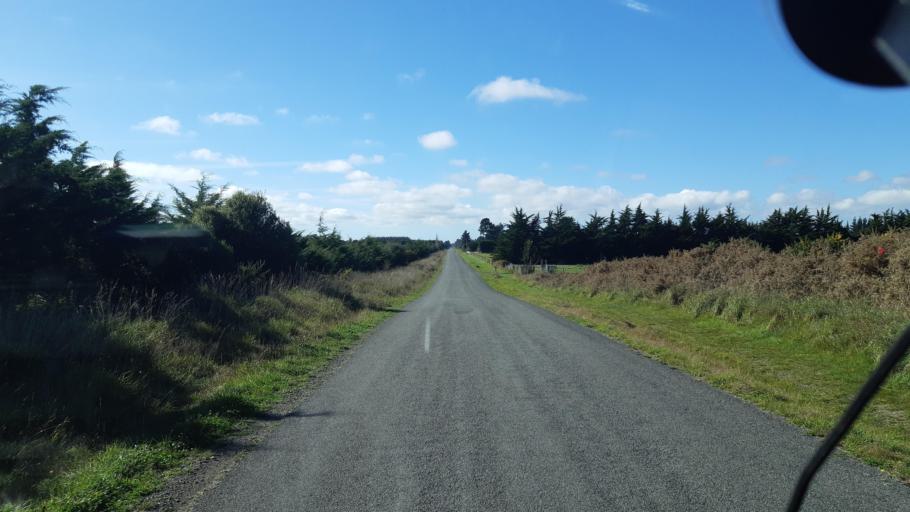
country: NZ
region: Canterbury
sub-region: Waimakariri District
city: Woodend
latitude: -43.2665
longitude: 172.4982
